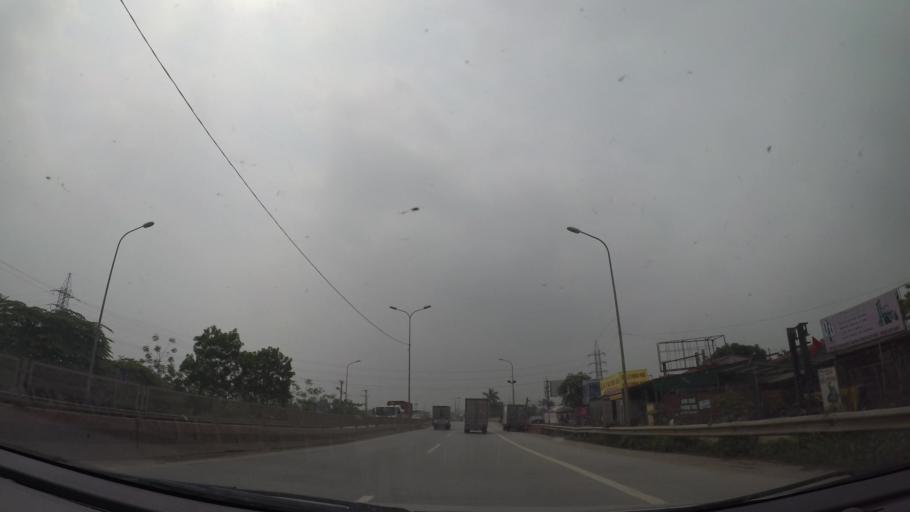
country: VN
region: Ha Noi
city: Tay Ho
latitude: 21.1171
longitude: 105.7840
